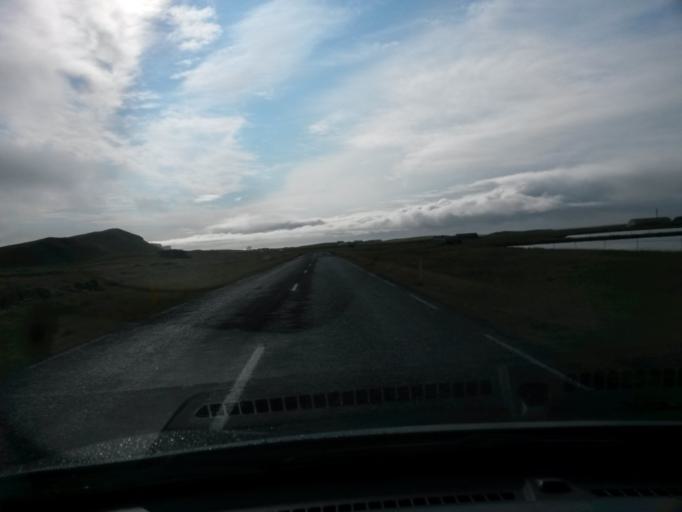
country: IS
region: South
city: Vestmannaeyjar
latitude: 63.4368
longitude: -19.1937
